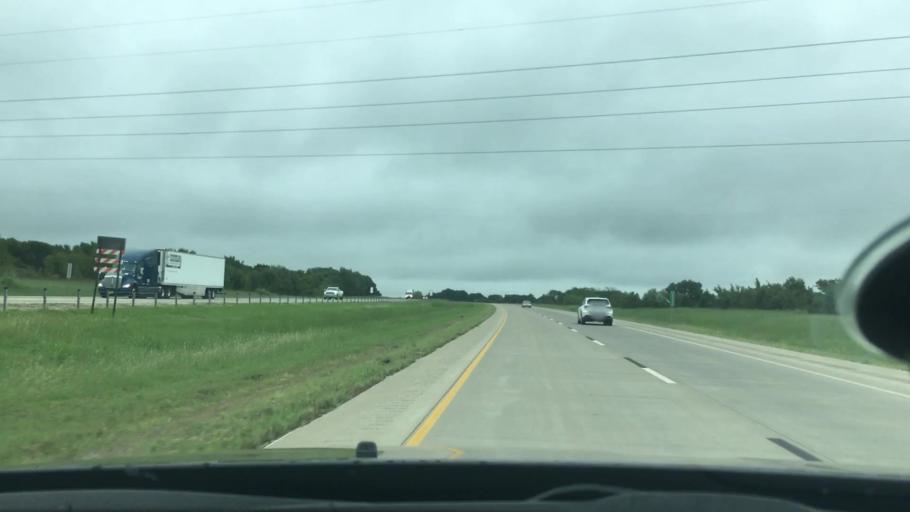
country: US
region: Oklahoma
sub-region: Okmulgee County
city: Wilson
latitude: 35.4285
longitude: -96.1011
